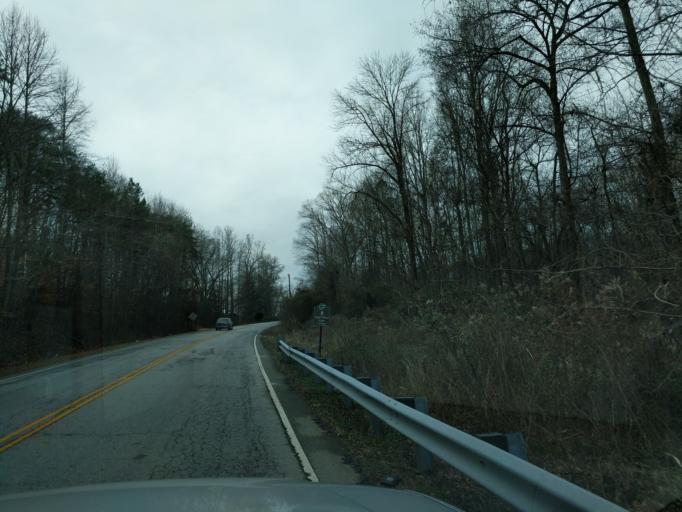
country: US
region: South Carolina
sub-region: Spartanburg County
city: Wellford
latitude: 34.8724
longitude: -82.0817
